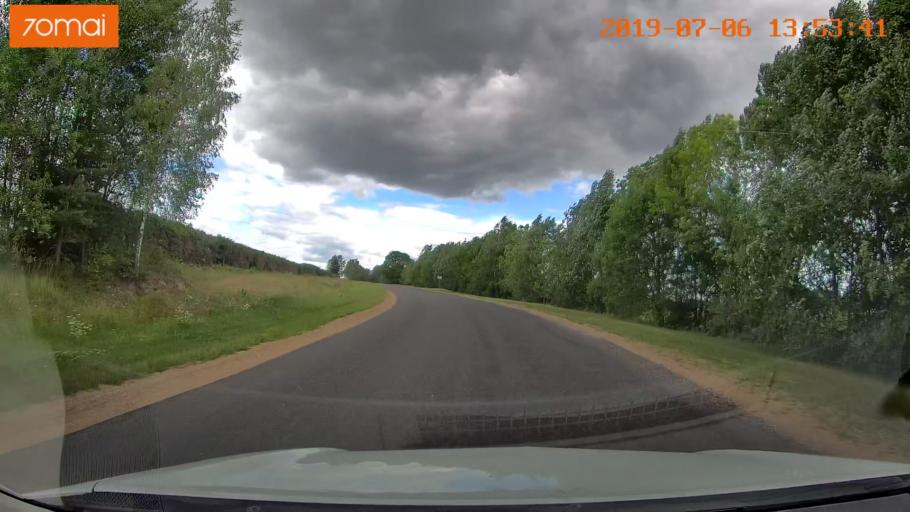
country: BY
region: Minsk
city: Ivyanyets
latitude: 53.7370
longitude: 26.8247
